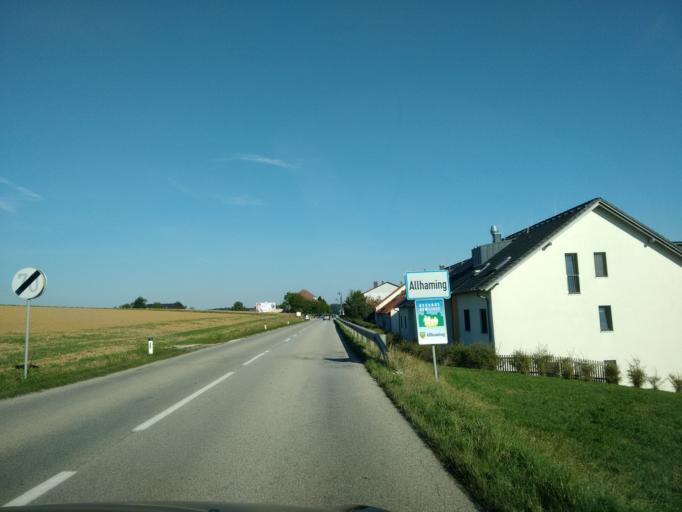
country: AT
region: Upper Austria
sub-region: Wels-Land
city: Marchtrenk
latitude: 48.1530
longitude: 14.1647
